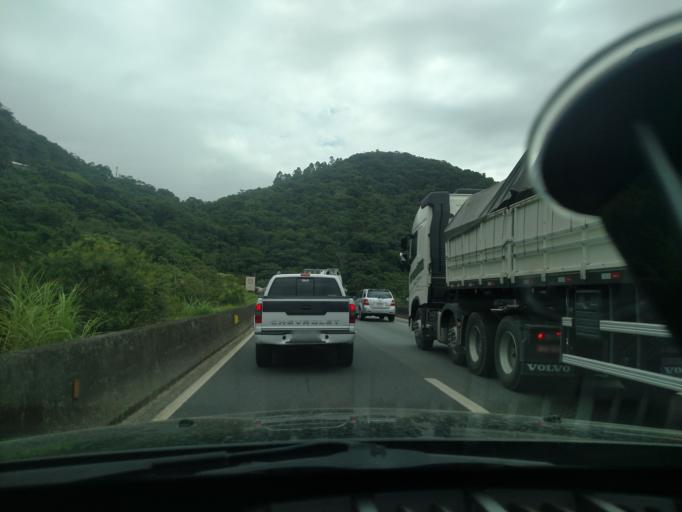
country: BR
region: Santa Catarina
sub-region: Itapema
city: Itapema
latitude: -27.0503
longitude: -48.5977
